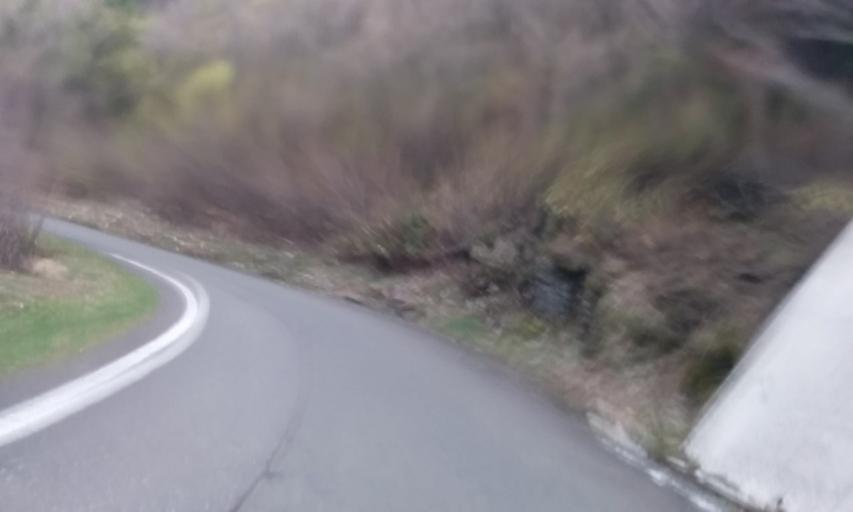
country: JP
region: Ehime
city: Saijo
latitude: 33.7822
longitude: 133.2162
